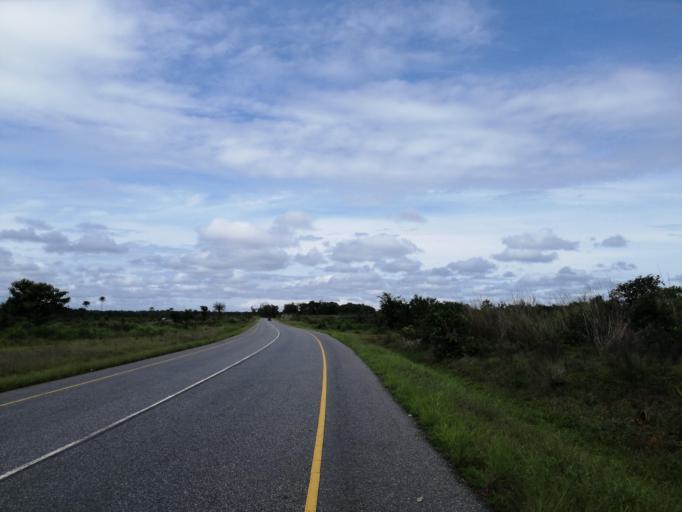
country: SL
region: Northern Province
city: Port Loko
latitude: 8.7343
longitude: -12.9490
